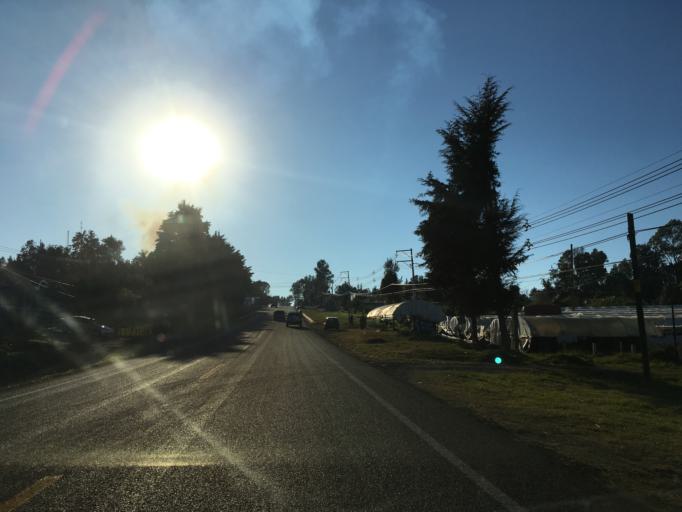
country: MX
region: Michoacan
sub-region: Zitacuaro
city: San Felipe los Alzati (Colonia Nueva)
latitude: 19.4866
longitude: -100.3850
